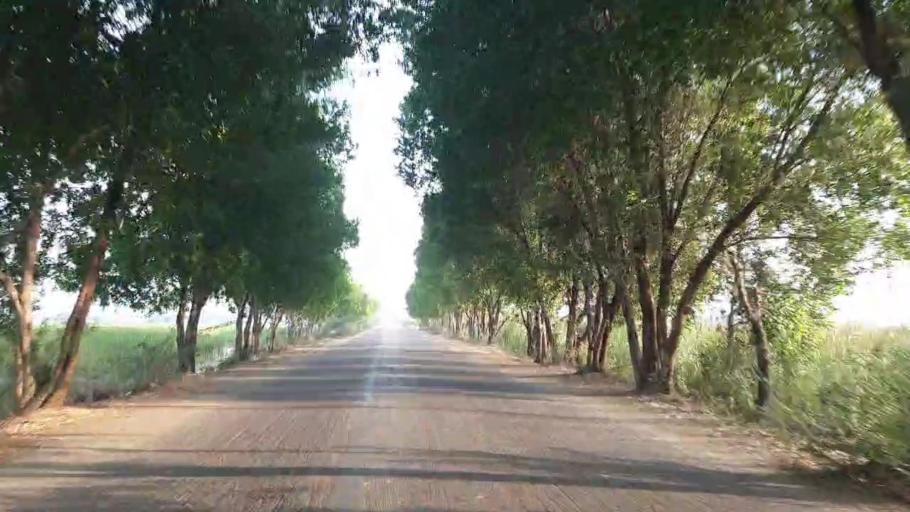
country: PK
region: Sindh
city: Tando Bago
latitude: 24.7359
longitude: 68.9456
